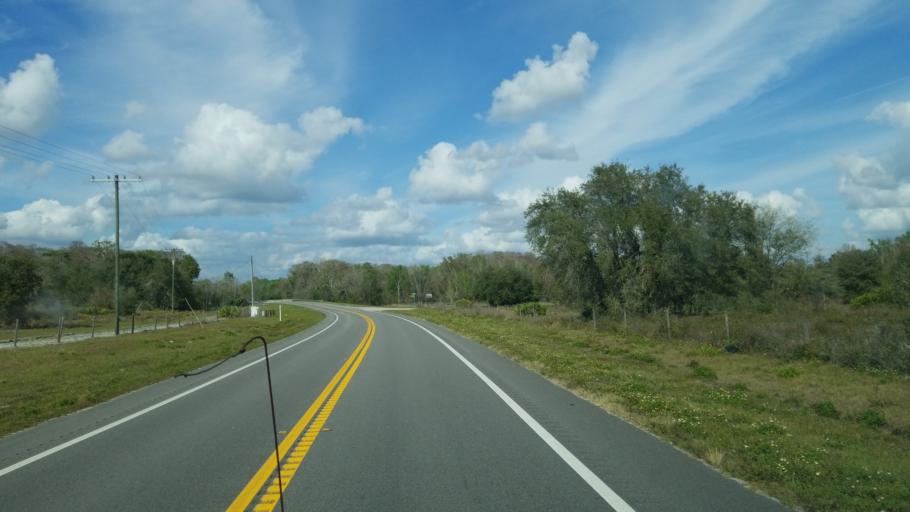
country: US
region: Florida
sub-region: Brevard County
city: June Park
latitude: 27.9411
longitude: -80.9960
